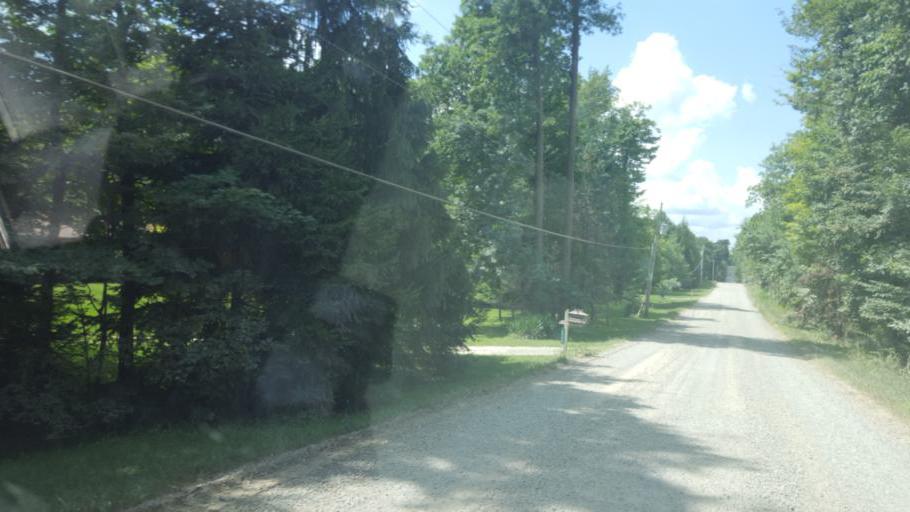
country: US
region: Ohio
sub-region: Morrow County
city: Mount Gilead
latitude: 40.4328
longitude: -82.7784
